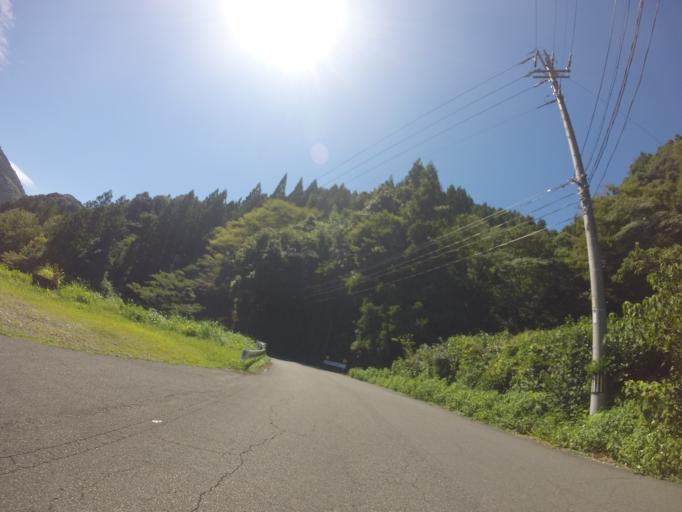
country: JP
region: Shizuoka
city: Fujieda
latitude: 34.9559
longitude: 138.2085
